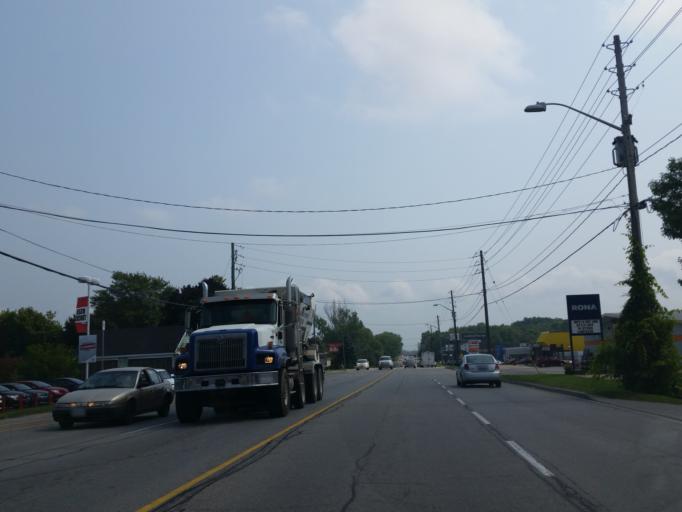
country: CA
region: Ontario
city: Brockville
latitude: 44.6041
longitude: -75.7148
